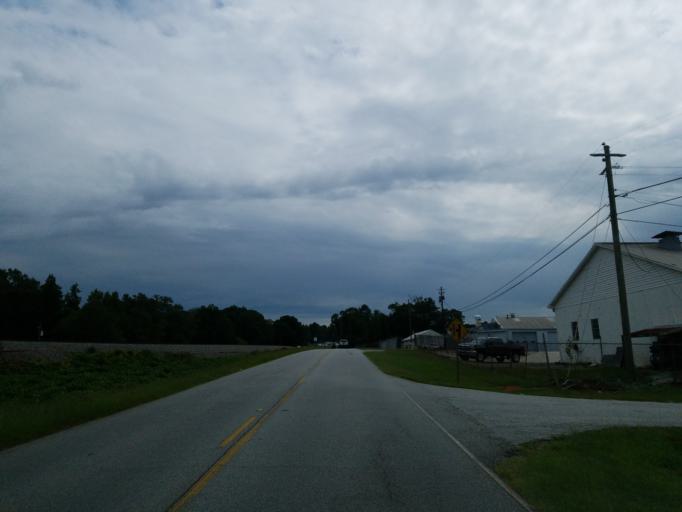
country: US
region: Georgia
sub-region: Spalding County
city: Experiment
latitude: 33.3067
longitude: -84.2890
